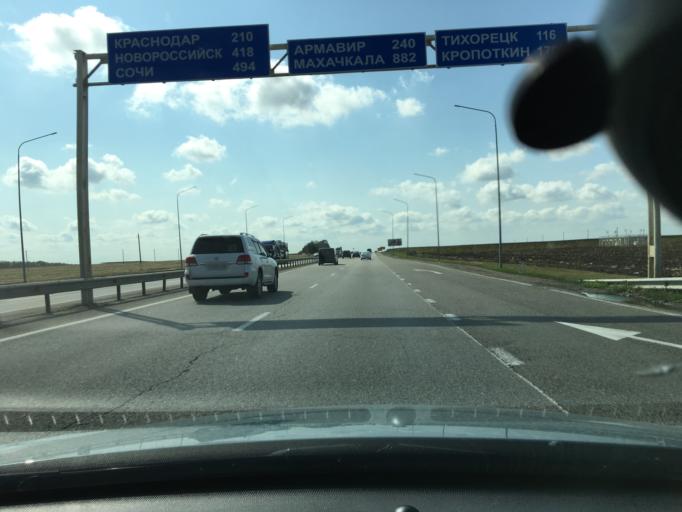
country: RU
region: Krasnodarskiy
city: Krasnoye
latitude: 46.7865
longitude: 39.6658
